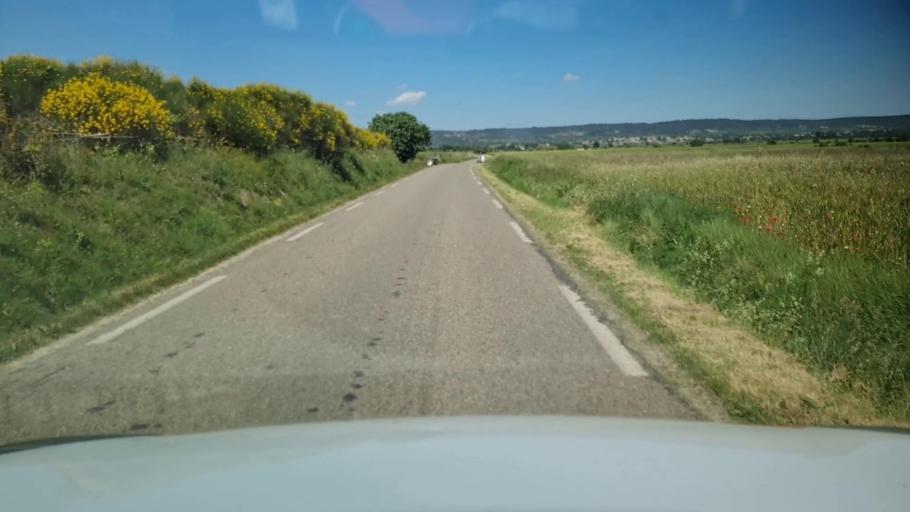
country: FR
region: Languedoc-Roussillon
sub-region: Departement du Gard
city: Calvisson
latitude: 43.7994
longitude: 4.1937
